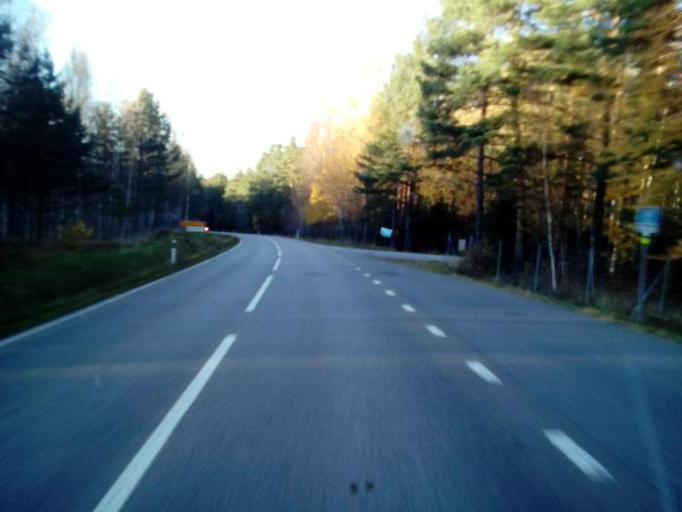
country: SE
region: OErebro
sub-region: Hallsbergs Kommun
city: Palsboda
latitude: 59.0071
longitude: 15.4024
